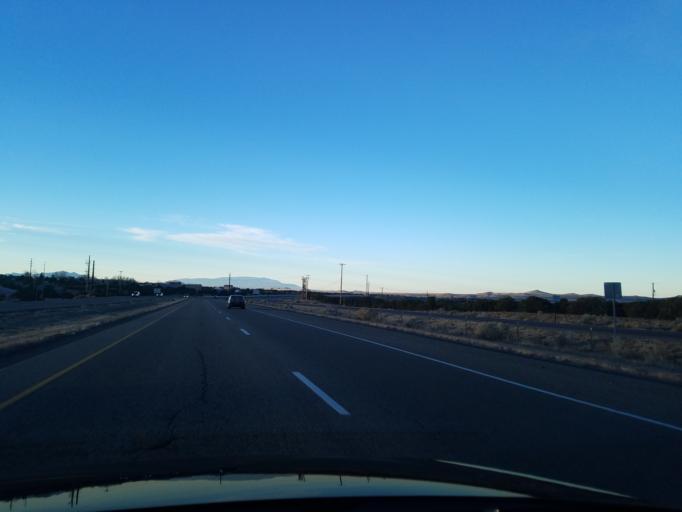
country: US
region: New Mexico
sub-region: Santa Fe County
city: Agua Fria
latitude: 35.6711
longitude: -106.0172
